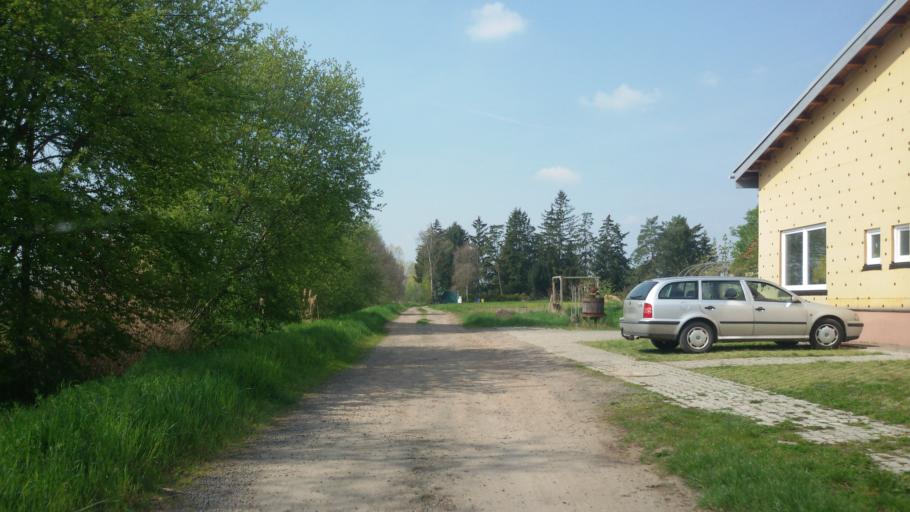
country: DE
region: Rheinland-Pfalz
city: Gerolsheim
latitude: 49.5622
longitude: 8.2601
